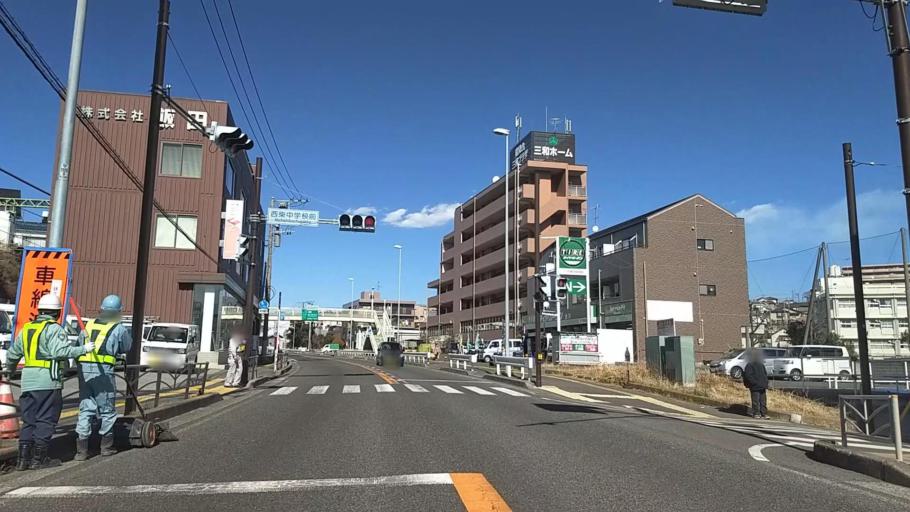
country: JP
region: Kanagawa
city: Zushi
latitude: 35.3524
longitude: 139.6277
